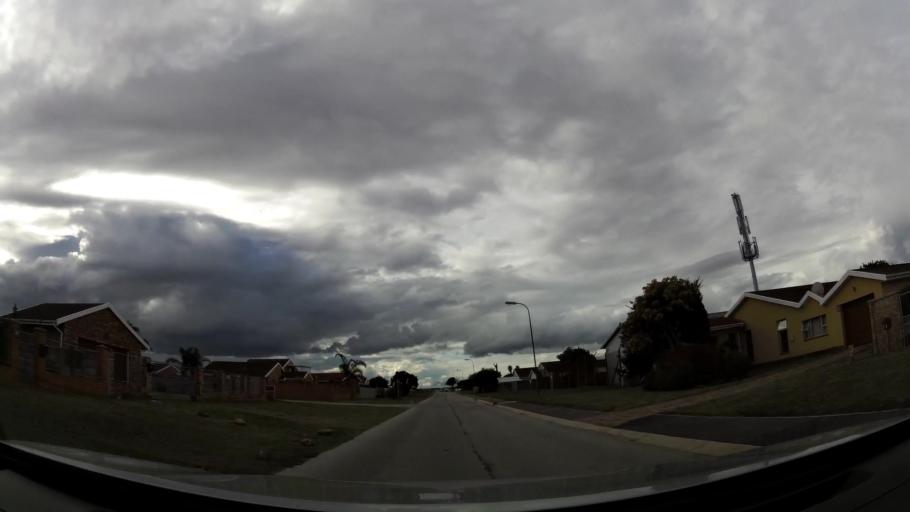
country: ZA
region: Eastern Cape
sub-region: Nelson Mandela Bay Metropolitan Municipality
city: Port Elizabeth
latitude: -33.9373
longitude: 25.4634
